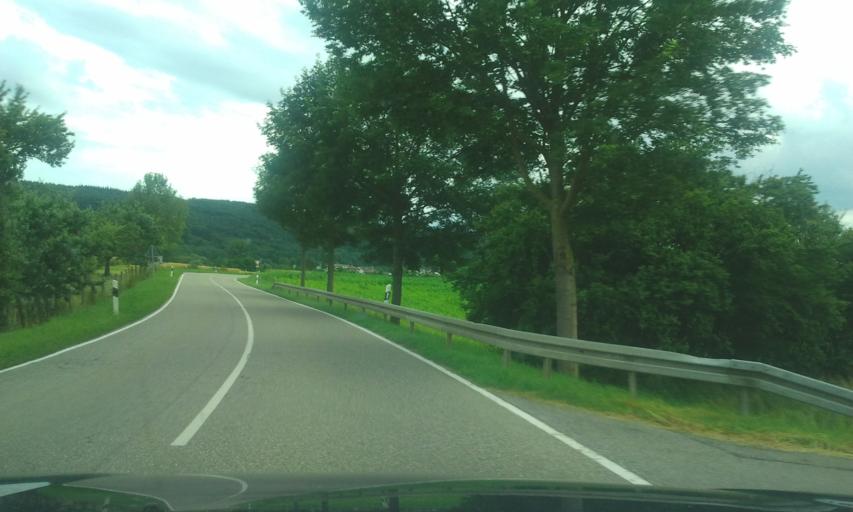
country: DE
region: Baden-Wuerttemberg
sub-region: Karlsruhe Region
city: Muhlacker
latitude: 48.9406
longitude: 8.8755
